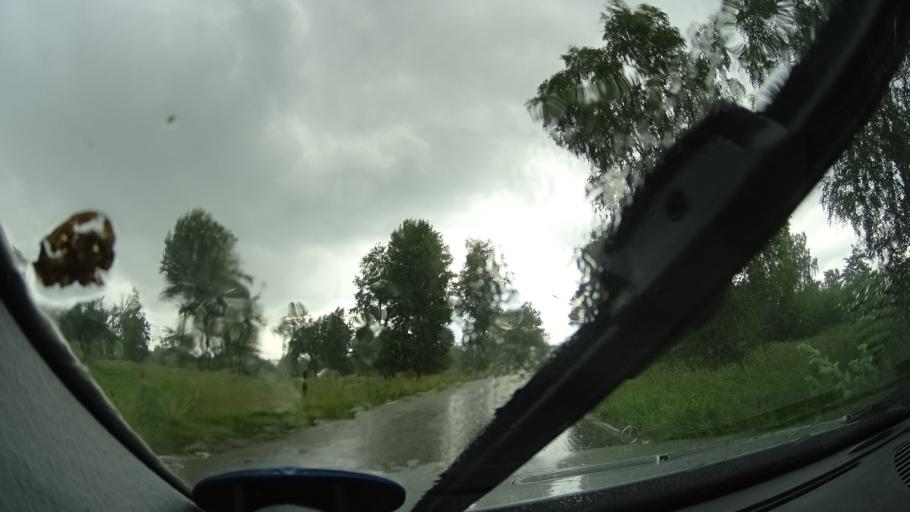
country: SE
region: Kalmar
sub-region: Emmaboda Kommun
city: Emmaboda
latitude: 56.6145
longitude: 15.5791
